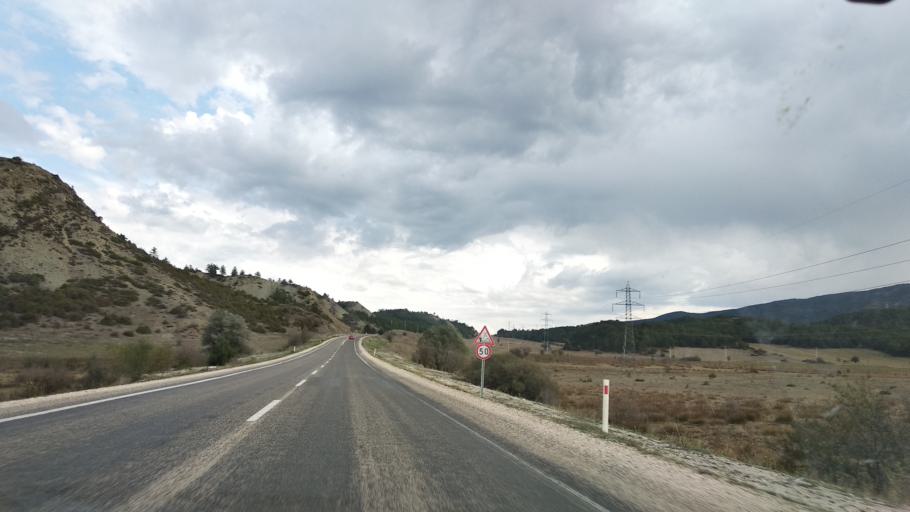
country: TR
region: Bolu
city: Mudurnu
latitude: 40.4816
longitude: 31.1753
